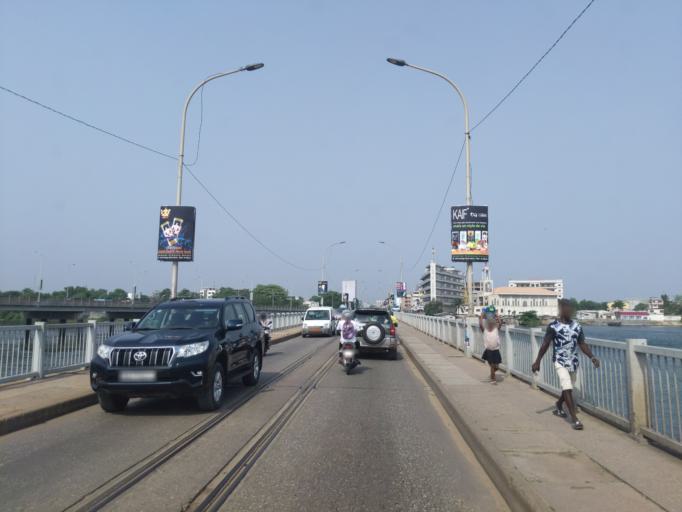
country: BJ
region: Littoral
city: Cotonou
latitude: 6.3587
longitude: 2.4417
